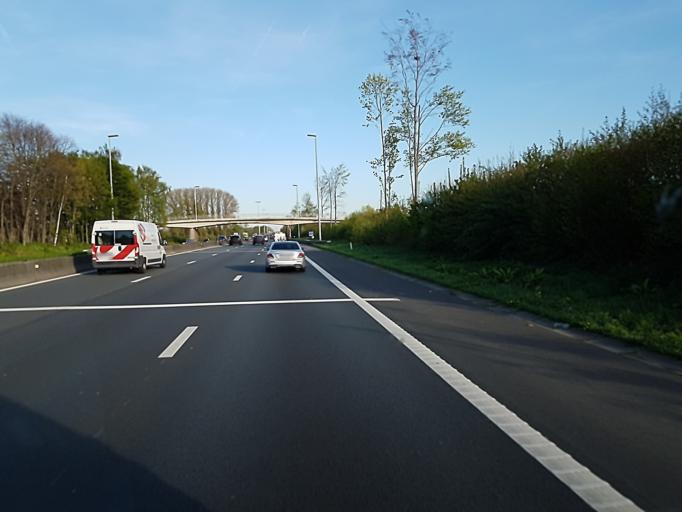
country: BE
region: Flanders
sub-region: Provincie Oost-Vlaanderen
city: Sint-Lievens-Houtem
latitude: 50.9553
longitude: 3.8783
